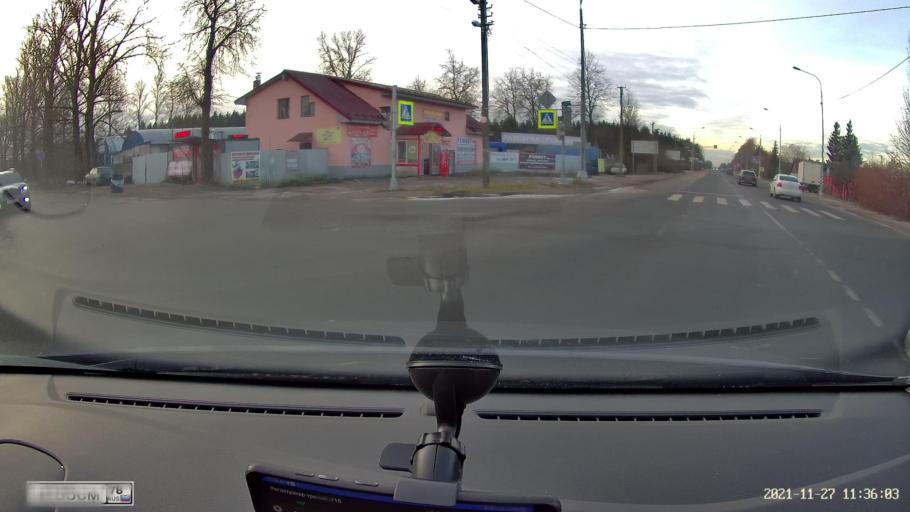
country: RU
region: Leningrad
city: Russko-Vysotskoye
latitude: 59.7013
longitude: 29.9775
